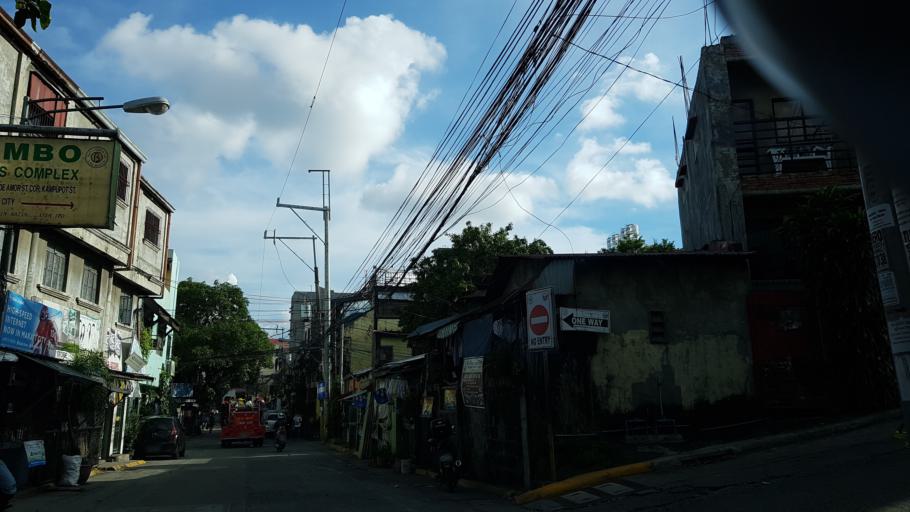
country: PH
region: Calabarzon
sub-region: Province of Rizal
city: Pateros
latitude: 14.5459
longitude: 121.0592
